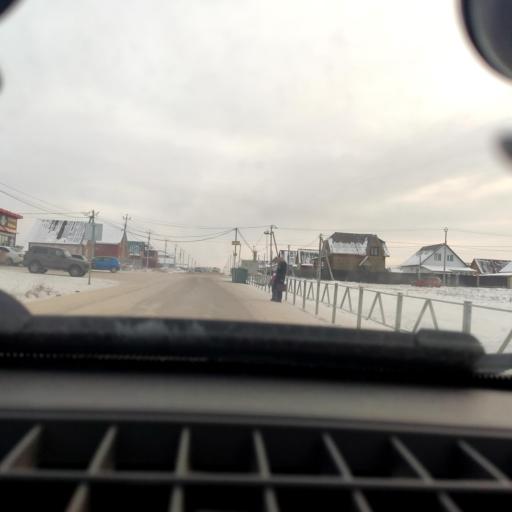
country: RU
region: Bashkortostan
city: Iglino
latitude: 54.8243
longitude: 56.4391
